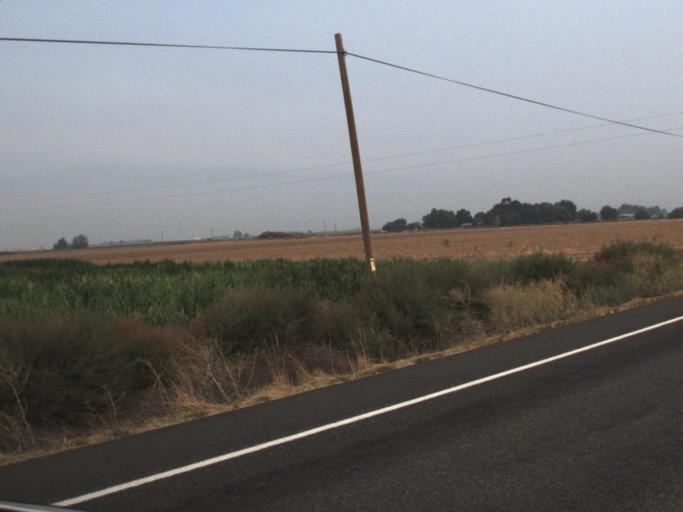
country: US
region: Washington
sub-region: Yakima County
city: Toppenish
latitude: 46.3270
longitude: -120.3204
